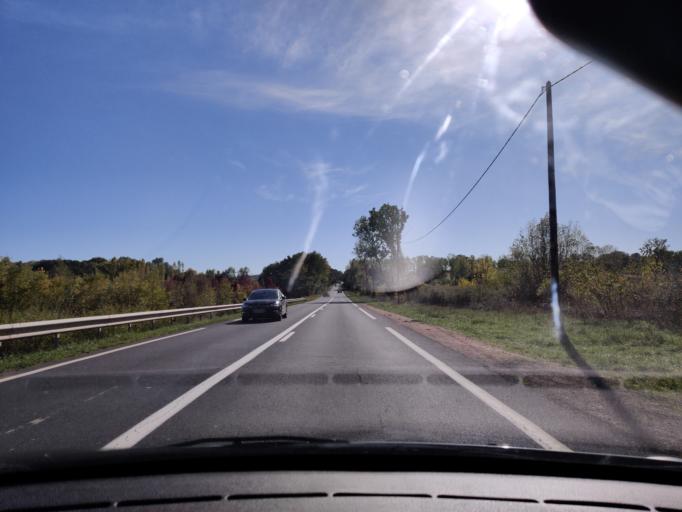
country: FR
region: Auvergne
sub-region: Departement du Puy-de-Dome
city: Combronde
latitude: 46.0105
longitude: 3.0910
